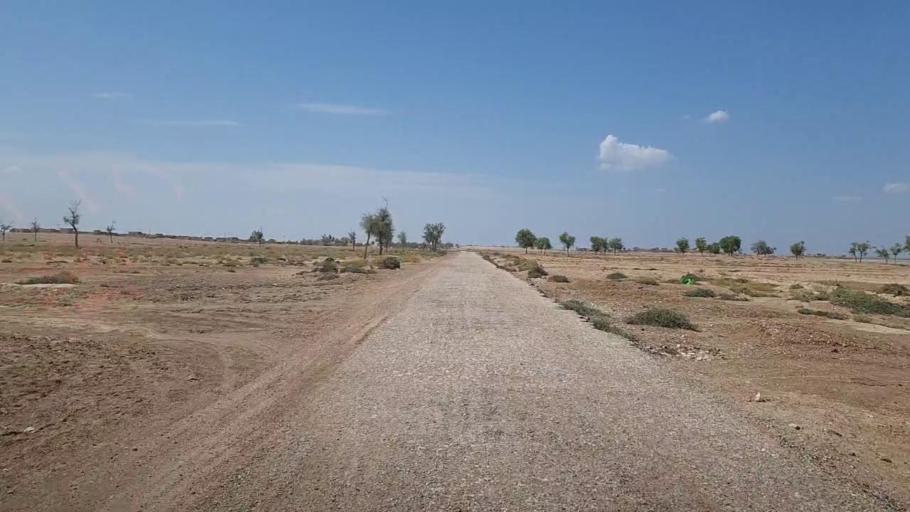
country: PK
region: Sindh
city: Sehwan
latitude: 26.3462
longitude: 67.6741
